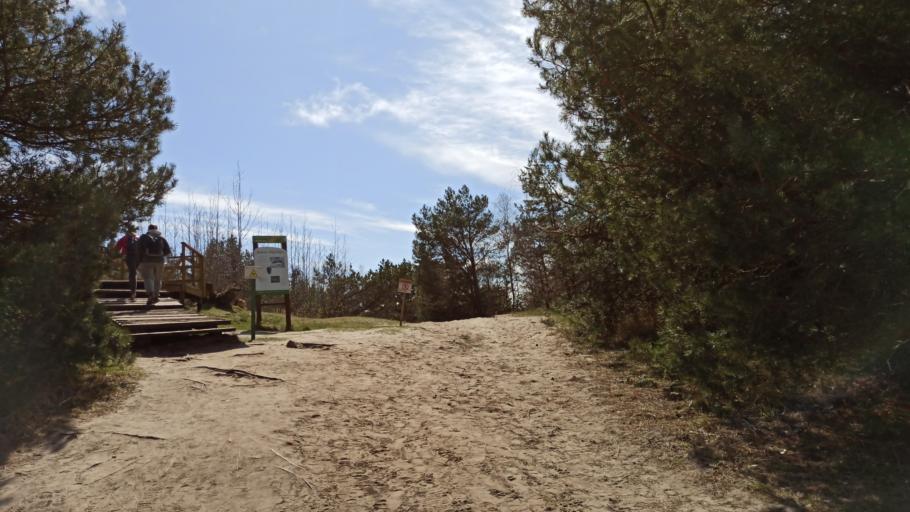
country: LT
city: Nida
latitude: 55.1487
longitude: 20.8119
